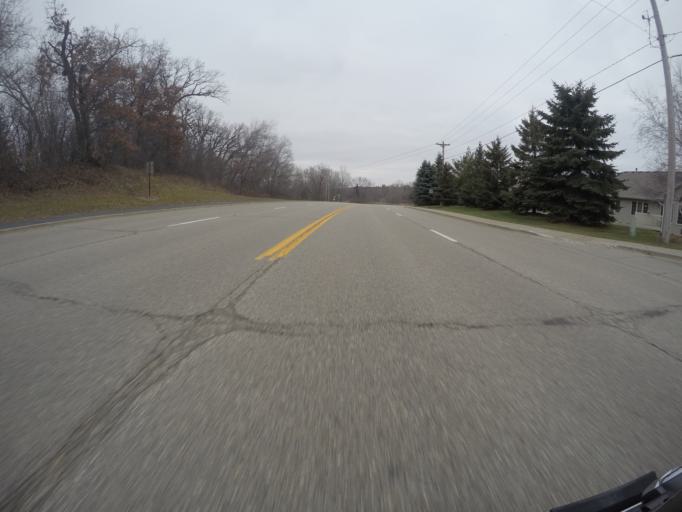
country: US
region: Minnesota
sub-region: Hennepin County
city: Eden Prairie
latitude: 44.8739
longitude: -93.4500
